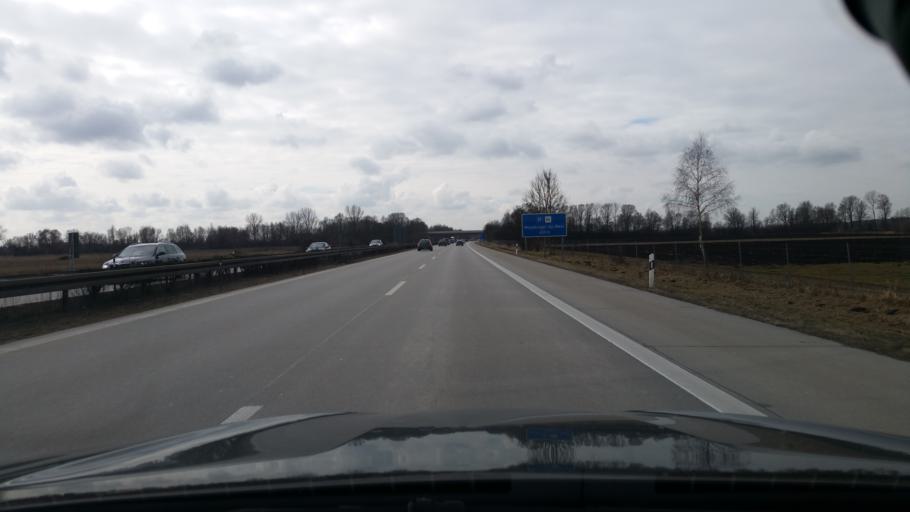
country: DE
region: Bavaria
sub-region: Upper Bavaria
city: Langenpreising
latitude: 48.4433
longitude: 11.9591
